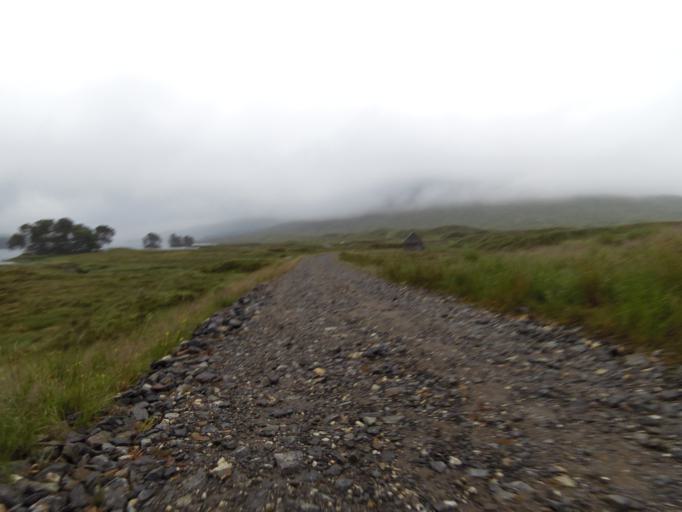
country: GB
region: Scotland
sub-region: Highland
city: Spean Bridge
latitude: 56.7655
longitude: -4.6690
